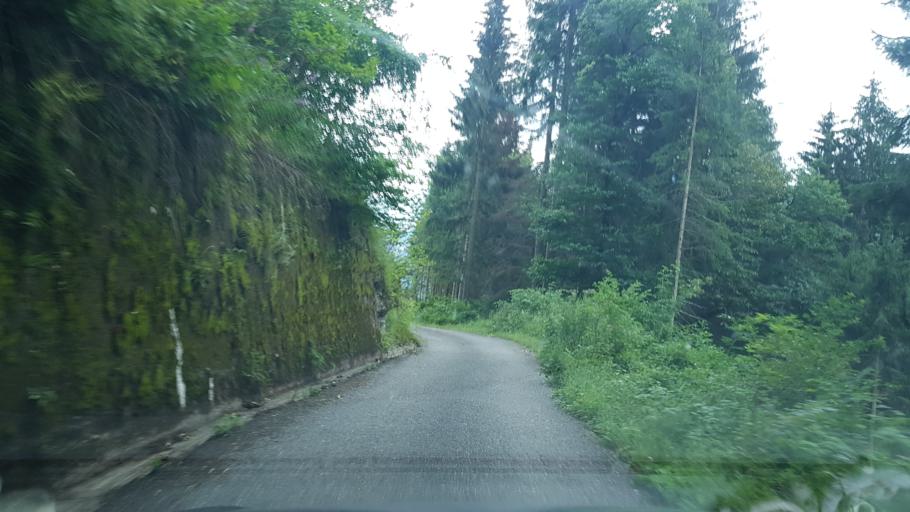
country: IT
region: Friuli Venezia Giulia
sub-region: Provincia di Udine
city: Cercivento
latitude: 46.5347
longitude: 12.9832
